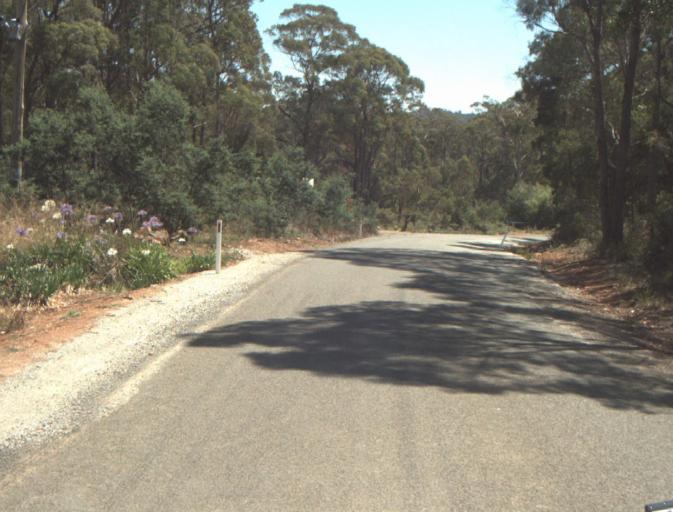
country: AU
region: Tasmania
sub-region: Launceston
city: Mayfield
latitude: -41.2809
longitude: 147.1190
